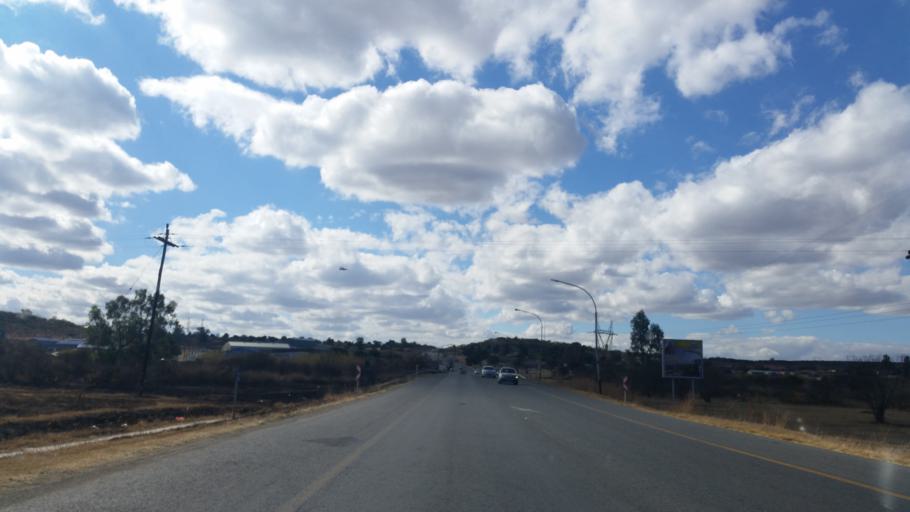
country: ZA
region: KwaZulu-Natal
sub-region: uThukela District Municipality
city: Ladysmith
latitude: -28.5389
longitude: 29.7978
